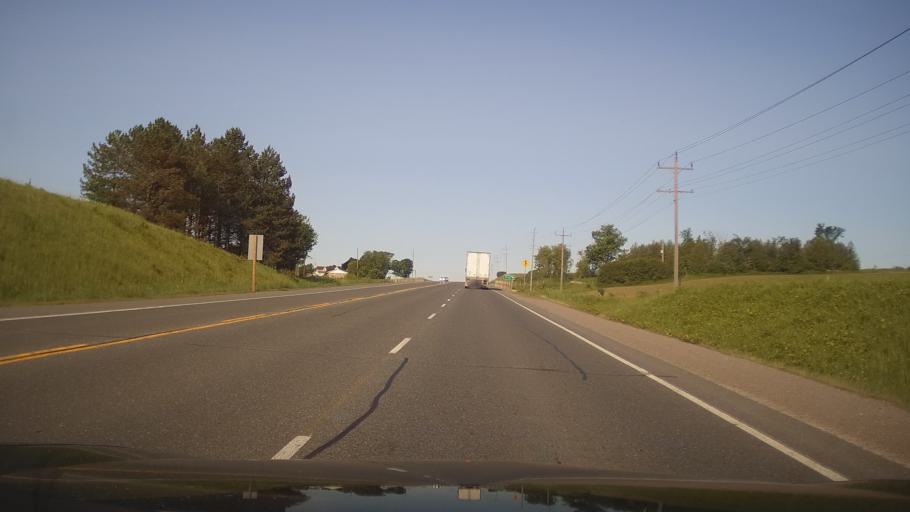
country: CA
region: Ontario
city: Peterborough
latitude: 44.3619
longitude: -78.0197
